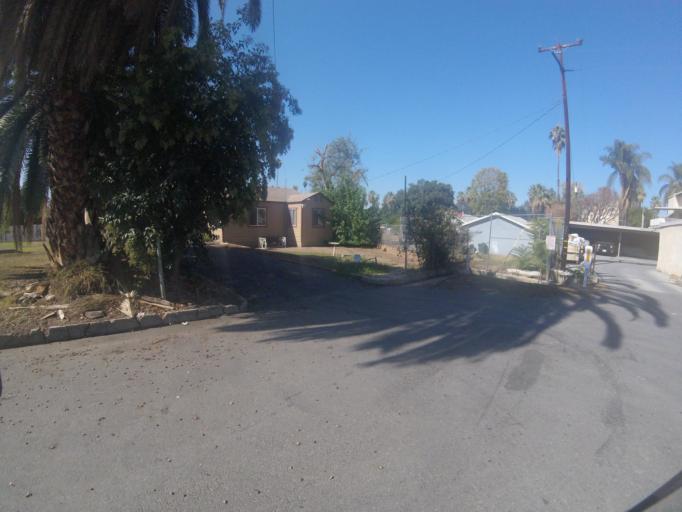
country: US
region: California
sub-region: San Bernardino County
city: Redlands
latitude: 34.0509
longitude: -117.1915
